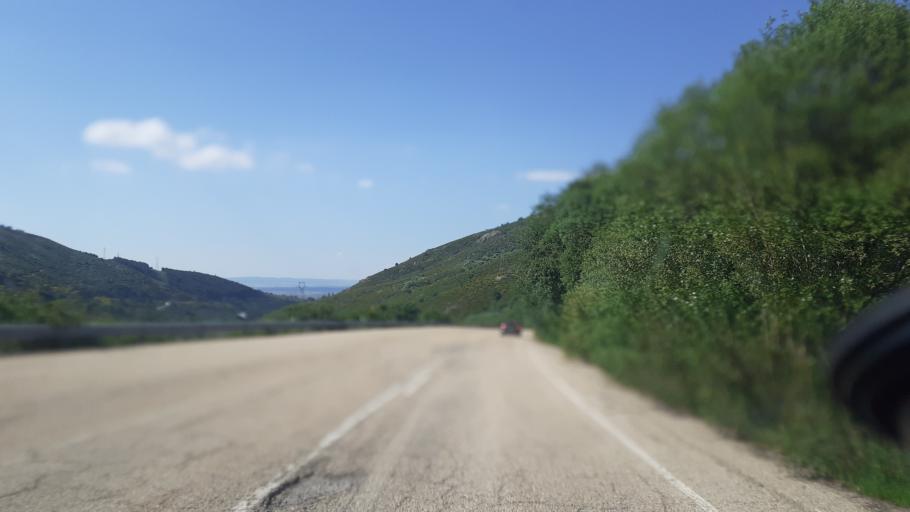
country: ES
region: Madrid
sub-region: Provincia de Madrid
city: Somosierra
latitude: 41.1415
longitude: -3.5786
